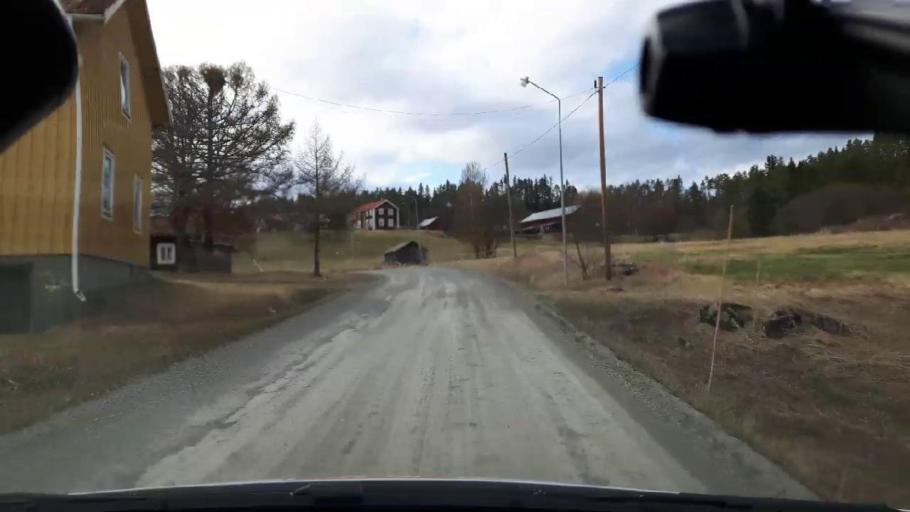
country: SE
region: Jaemtland
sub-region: OEstersunds Kommun
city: Brunflo
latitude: 62.9530
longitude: 14.6563
